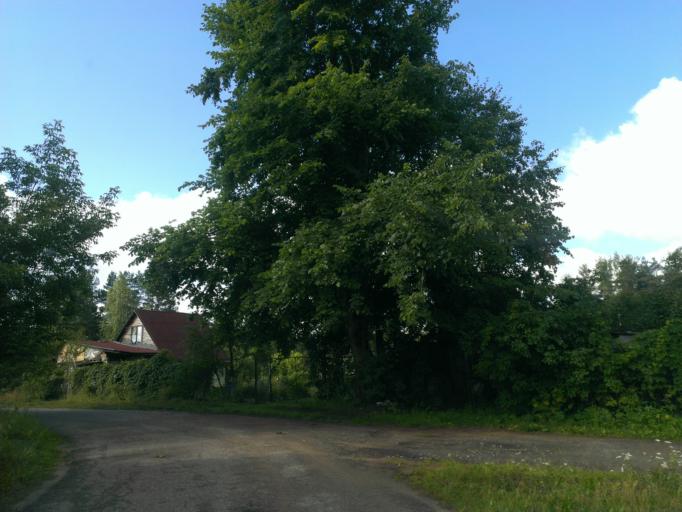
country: LV
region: Incukalns
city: Vangazi
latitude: 57.1030
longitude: 24.5256
